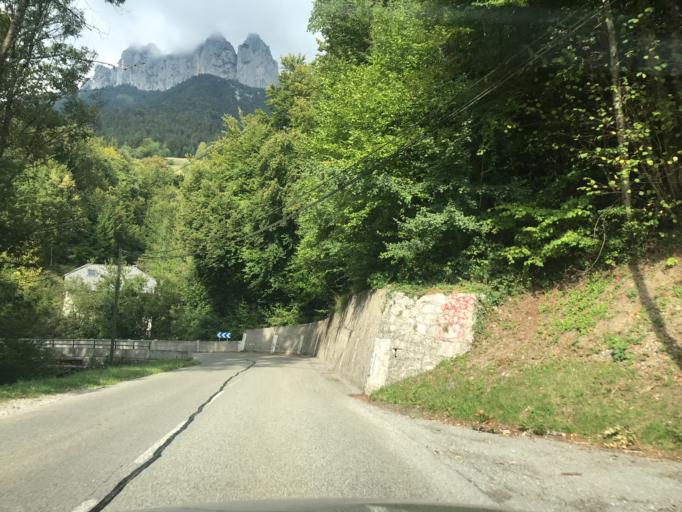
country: FR
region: Rhone-Alpes
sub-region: Departement de la Haute-Savoie
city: Talloires
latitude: 45.8415
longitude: 6.2257
